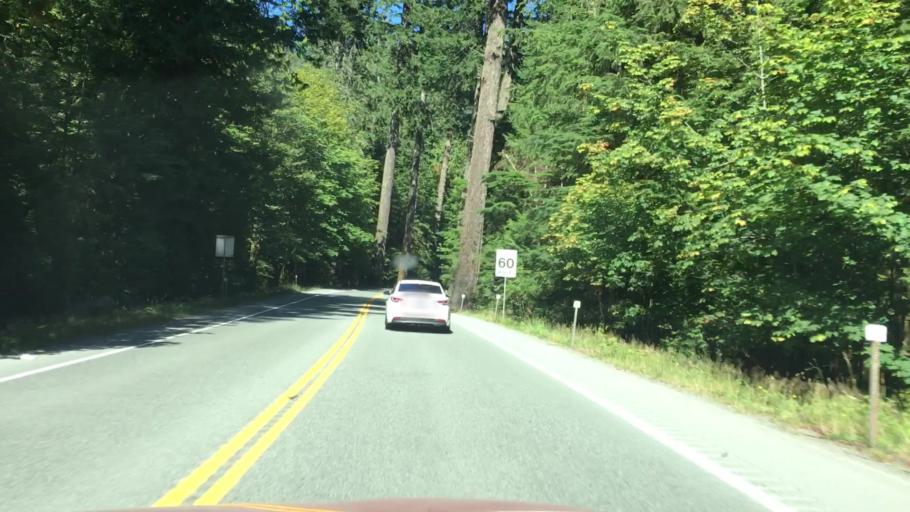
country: CA
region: British Columbia
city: Port Alberni
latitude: 49.2884
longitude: -124.6688
